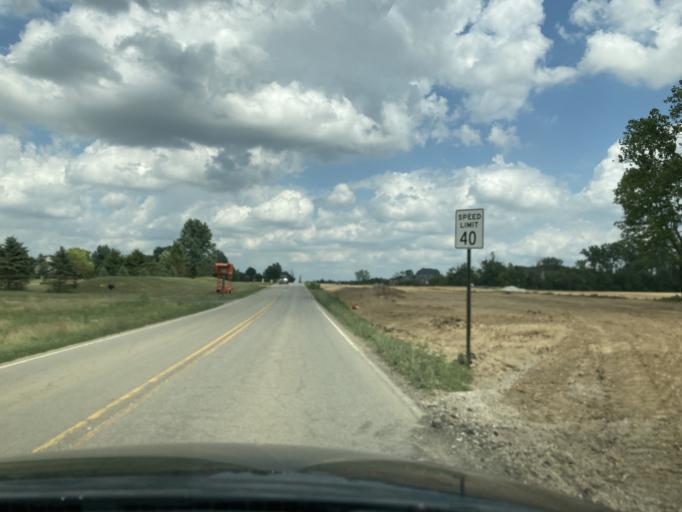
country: US
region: Indiana
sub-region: Boone County
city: Zionsville
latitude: 39.9987
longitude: -86.2342
